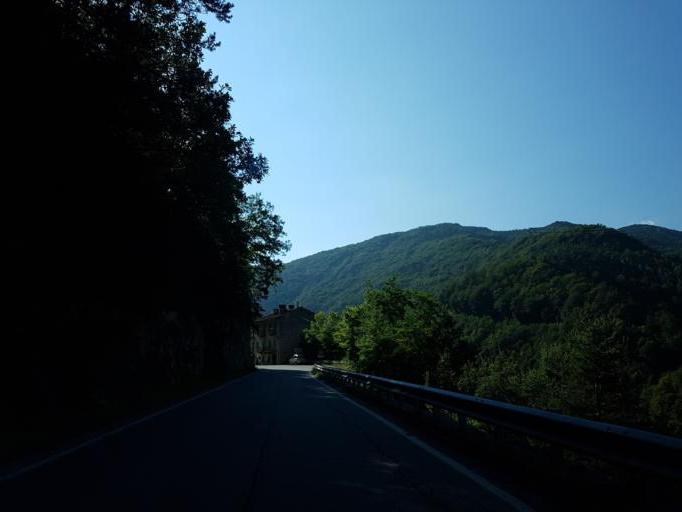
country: IT
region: Piedmont
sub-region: Provincia di Cuneo
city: Chiesa di Macra
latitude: 44.4929
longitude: 7.2143
